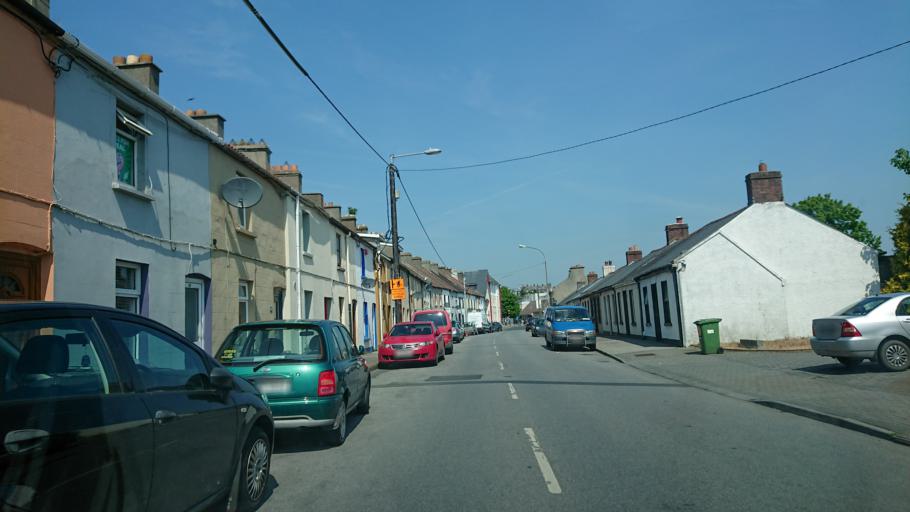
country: IE
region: Munster
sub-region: Waterford
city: Waterford
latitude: 52.2521
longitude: -7.1122
